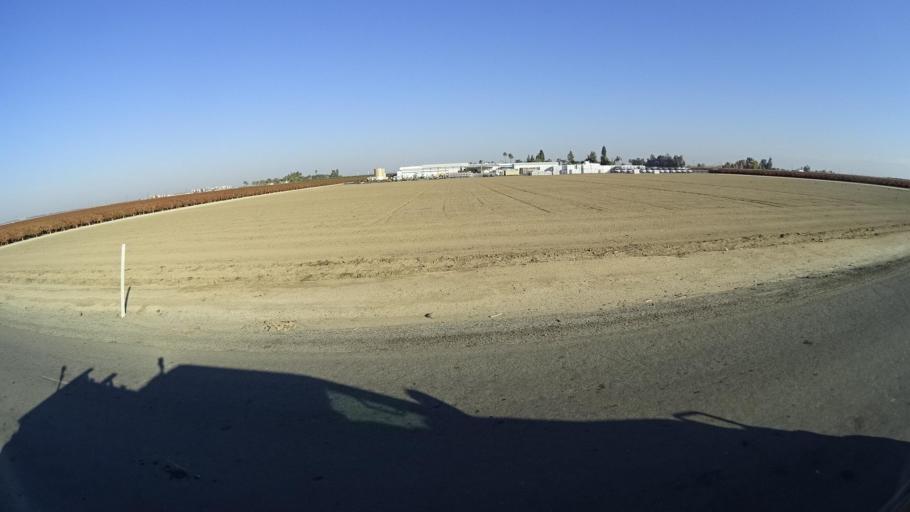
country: US
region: California
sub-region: Kern County
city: Delano
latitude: 35.7686
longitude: -119.1801
